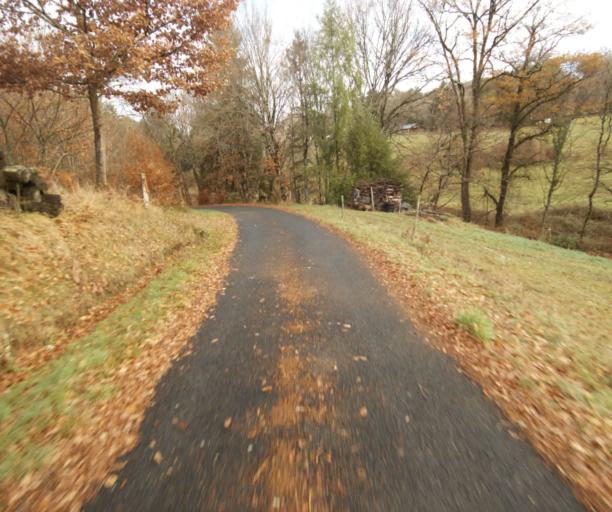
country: FR
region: Limousin
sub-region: Departement de la Correze
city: Saint-Mexant
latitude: 45.2523
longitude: 1.6412
